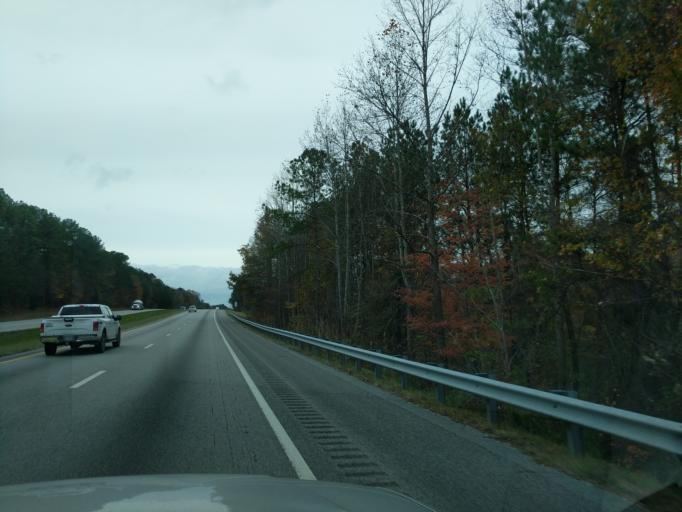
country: US
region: South Carolina
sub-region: Laurens County
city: Joanna
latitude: 34.4433
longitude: -81.7678
